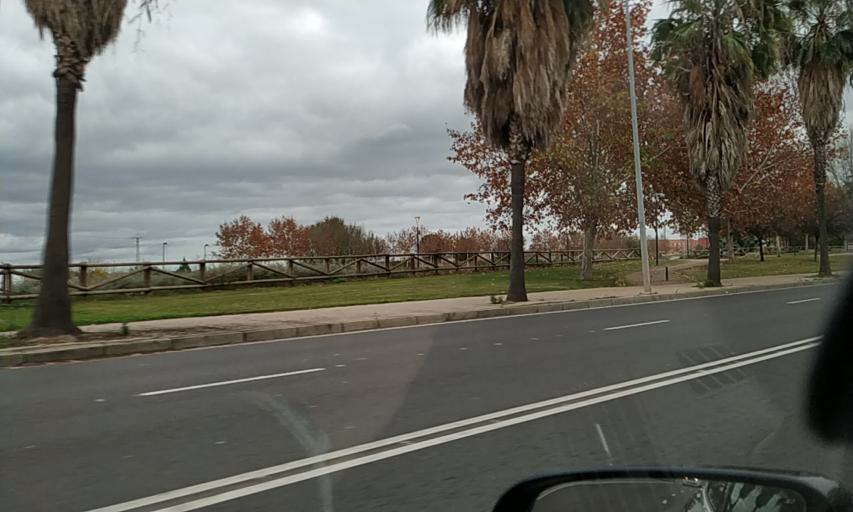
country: ES
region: Extremadura
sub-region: Provincia de Badajoz
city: Badajoz
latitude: 38.8839
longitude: -6.9663
